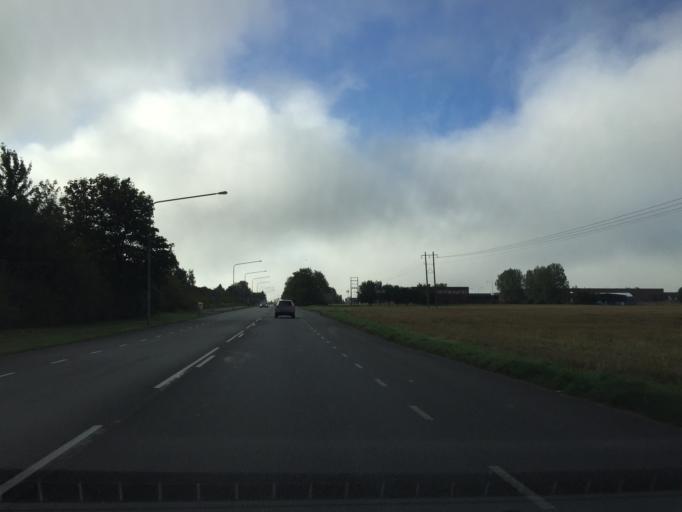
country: SE
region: Skane
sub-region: Staffanstorps Kommun
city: Staffanstorp
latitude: 55.6372
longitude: 13.1864
